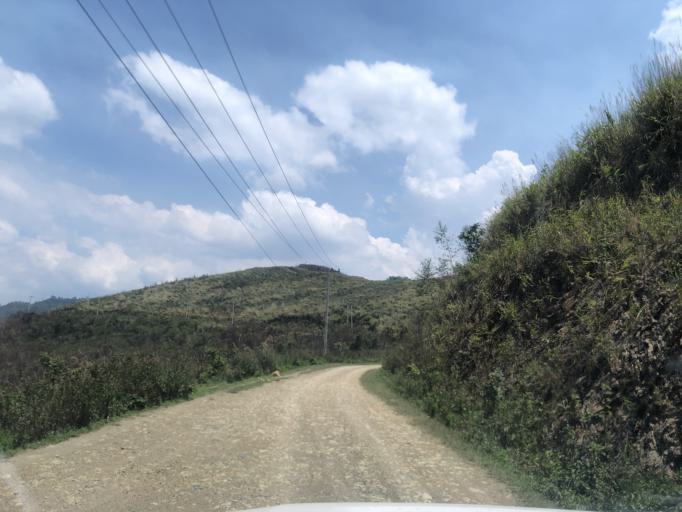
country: LA
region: Phongsali
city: Phongsali
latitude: 21.4044
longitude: 102.1858
